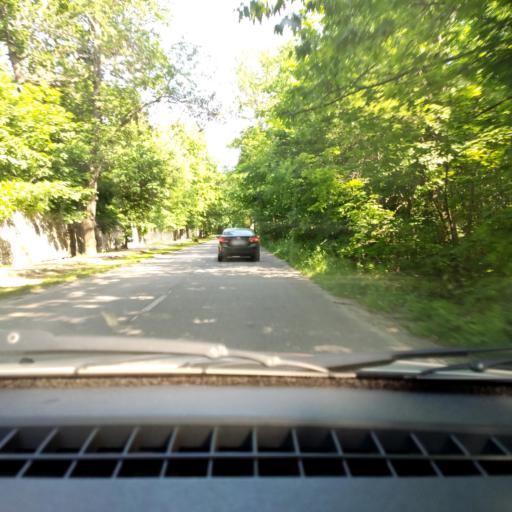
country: RU
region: Voronezj
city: Ramon'
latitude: 51.8228
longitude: 39.2632
